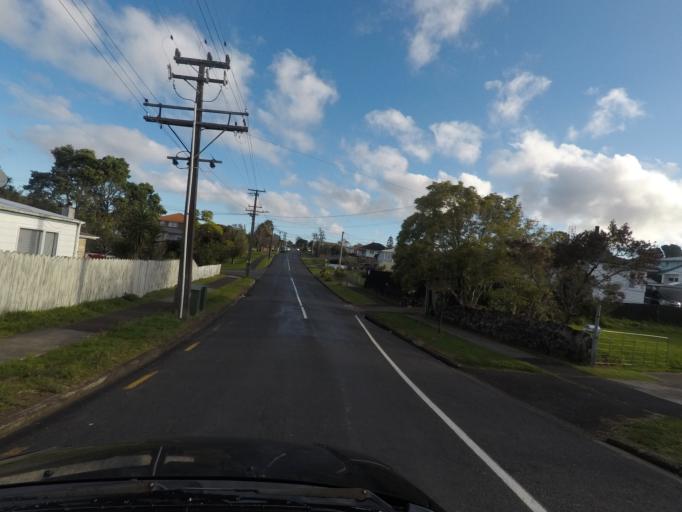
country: NZ
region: Auckland
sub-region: Auckland
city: Waitakere
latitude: -36.8994
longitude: 174.6687
